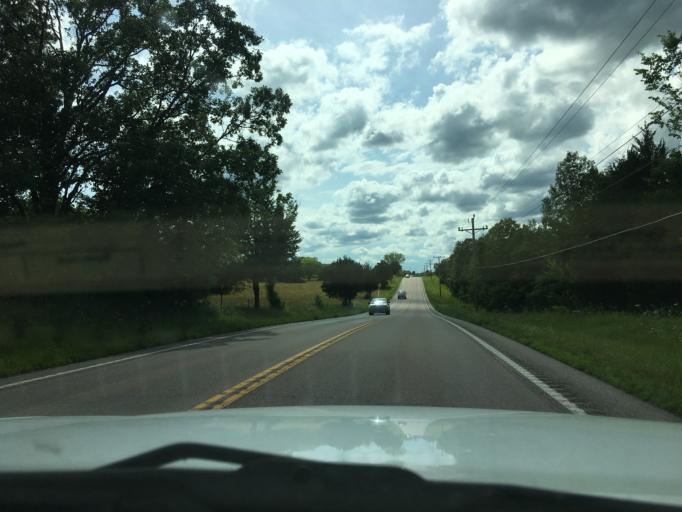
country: US
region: Missouri
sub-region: Franklin County
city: Gerald
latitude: 38.3875
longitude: -91.3854
